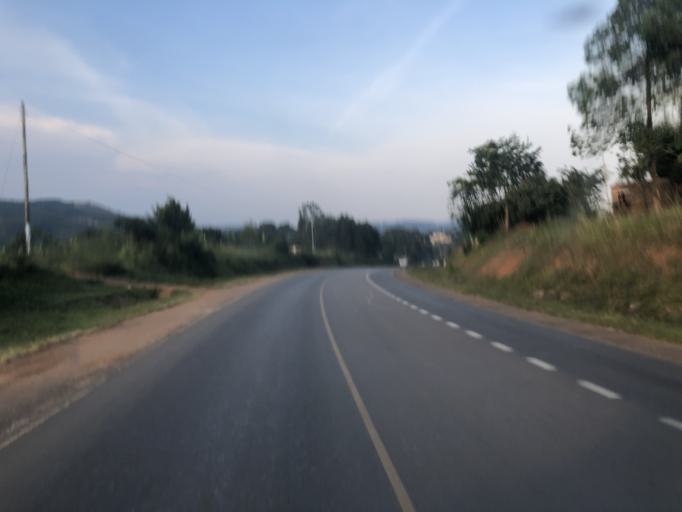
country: UG
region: Central Region
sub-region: Mpigi District
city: Mpigi
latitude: 0.2024
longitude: 32.3022
